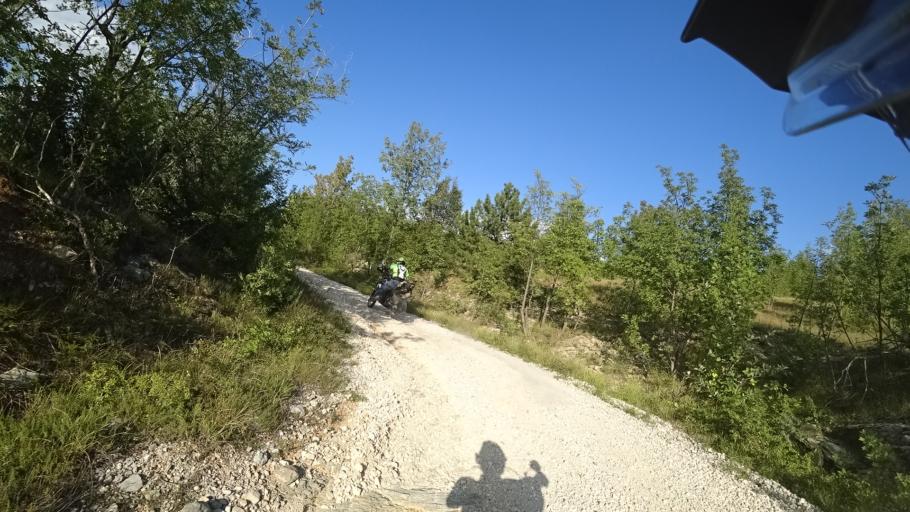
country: HR
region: Sibensko-Kniniska
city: Knin
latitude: 44.1651
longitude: 16.0823
